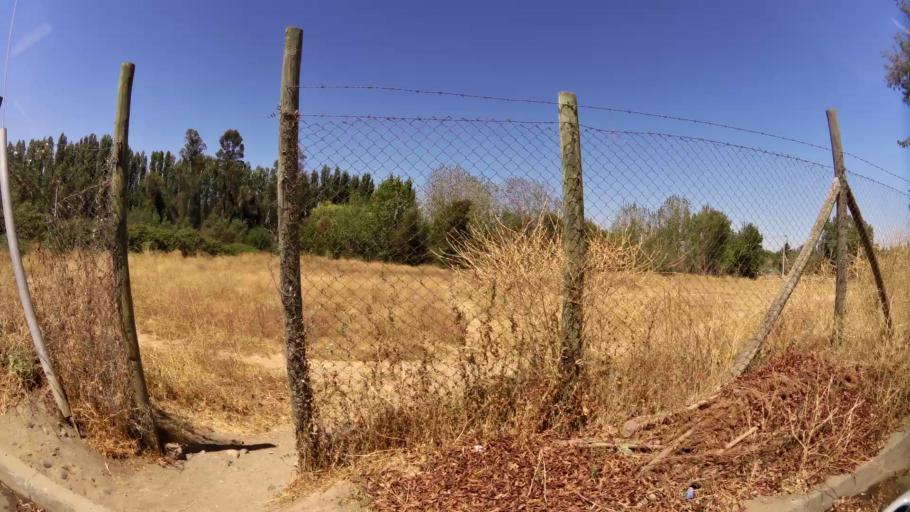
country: CL
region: Maule
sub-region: Provincia de Talca
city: Talca
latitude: -35.3078
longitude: -71.5099
